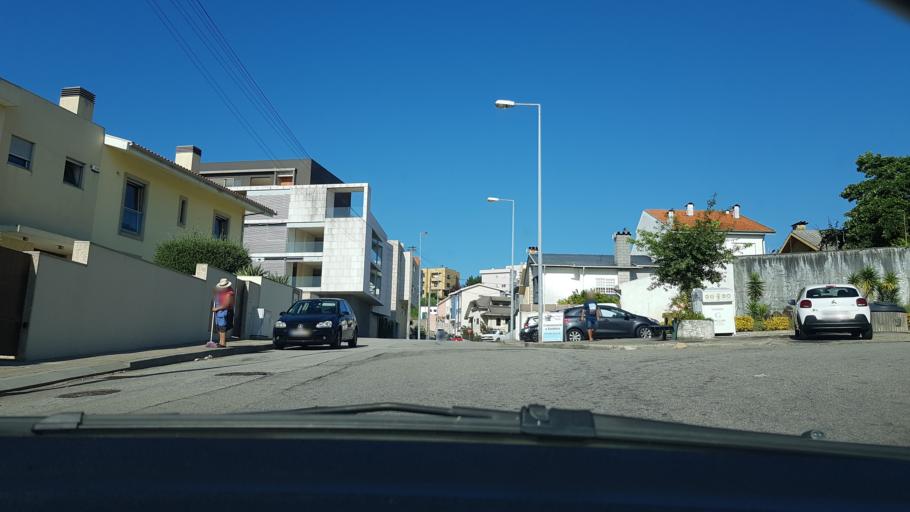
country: PT
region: Porto
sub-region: Gondomar
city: Baguim do Monte
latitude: 41.1892
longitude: -8.5272
